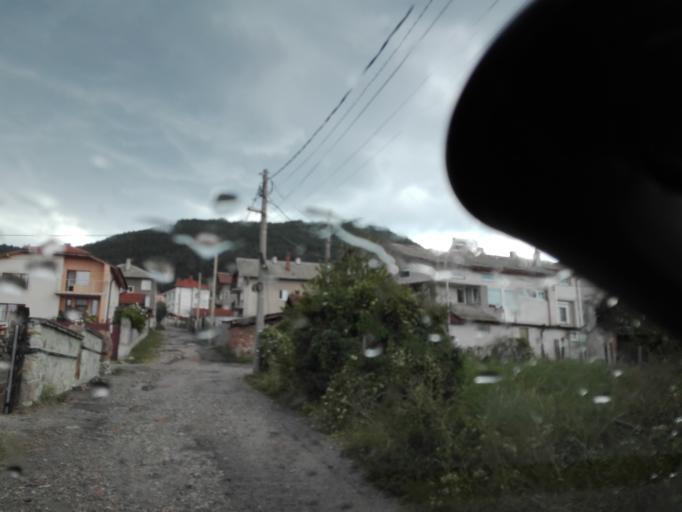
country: BG
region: Sofiya
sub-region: Obshtina Elin Pelin
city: Elin Pelin
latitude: 42.5991
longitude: 23.4845
